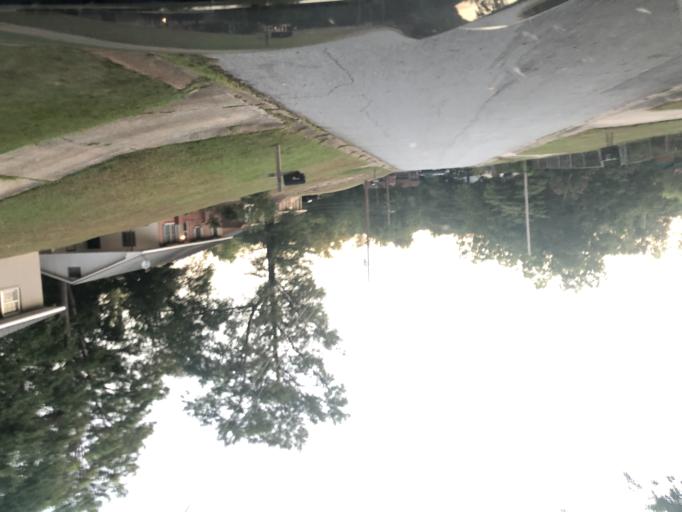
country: US
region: Georgia
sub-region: Muscogee County
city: Columbus
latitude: 32.4692
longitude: -84.8982
